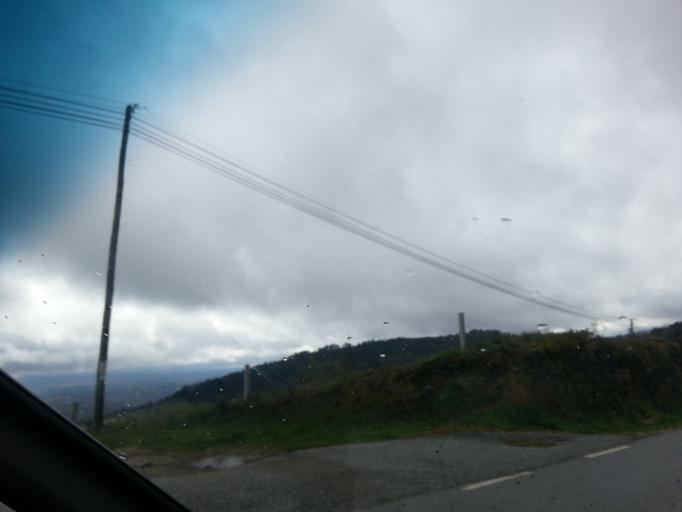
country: PT
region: Guarda
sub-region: Fornos de Algodres
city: Fornos de Algodres
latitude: 40.6151
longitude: -7.5484
